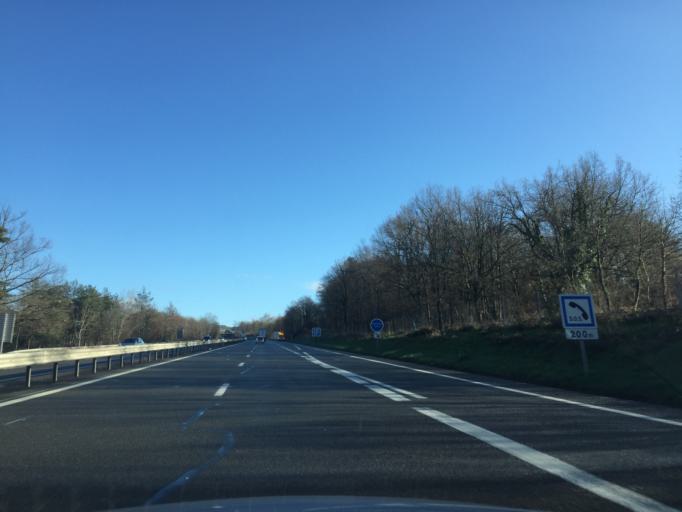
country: FR
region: Auvergne
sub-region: Departement du Puy-de-Dome
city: Peschadoires
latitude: 45.8612
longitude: 3.5086
